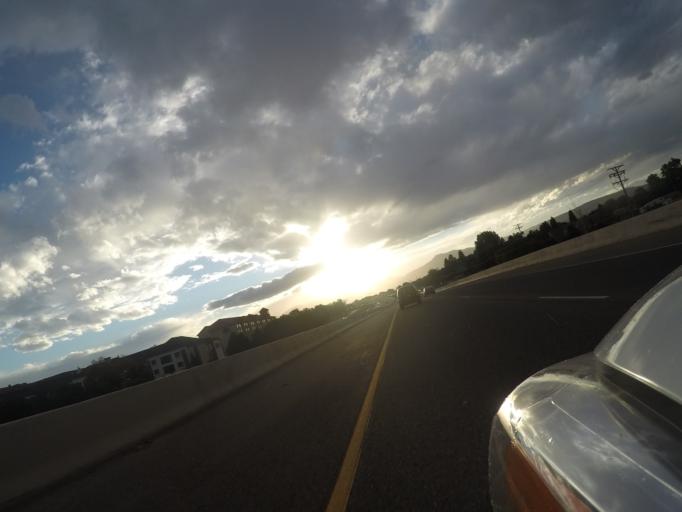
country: US
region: Colorado
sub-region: Arapahoe County
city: Sheridan
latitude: 39.6529
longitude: -105.0731
